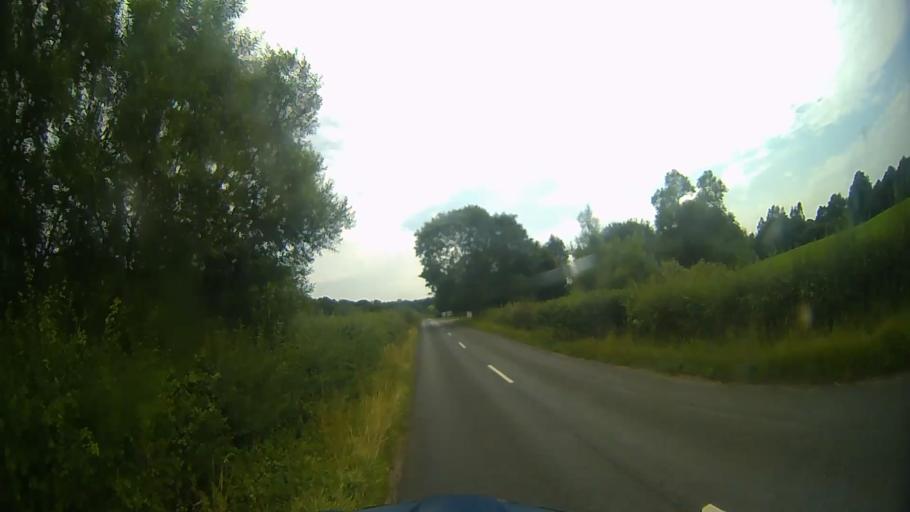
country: GB
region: England
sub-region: Hampshire
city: Kingsley
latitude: 51.1633
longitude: -0.8547
